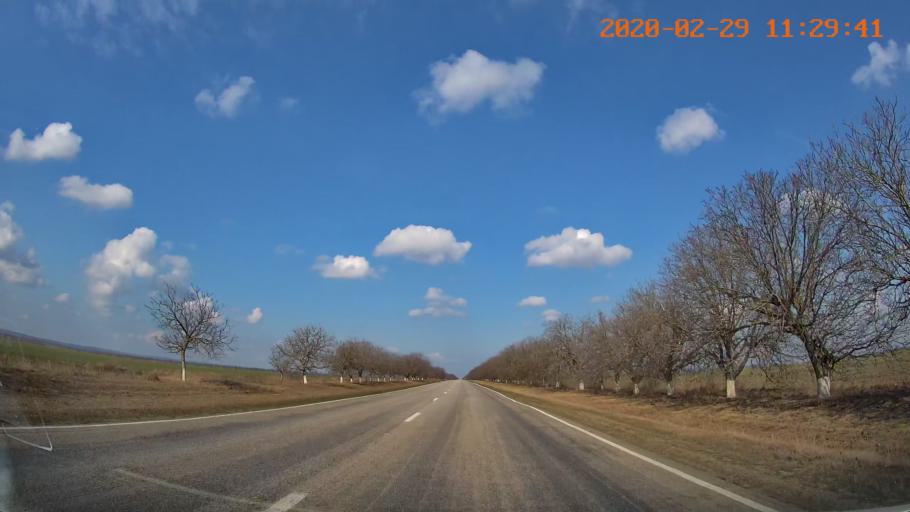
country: MD
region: Telenesti
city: Cocieri
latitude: 47.4983
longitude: 29.1232
